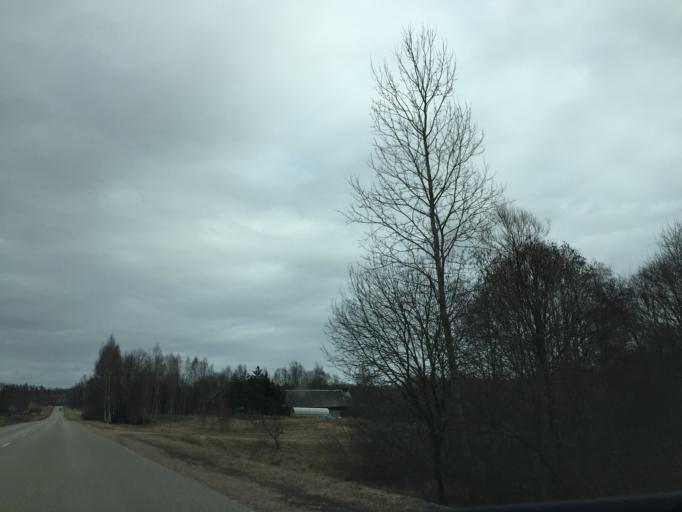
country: LV
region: Kraslavas Rajons
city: Kraslava
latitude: 55.9620
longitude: 27.1652
